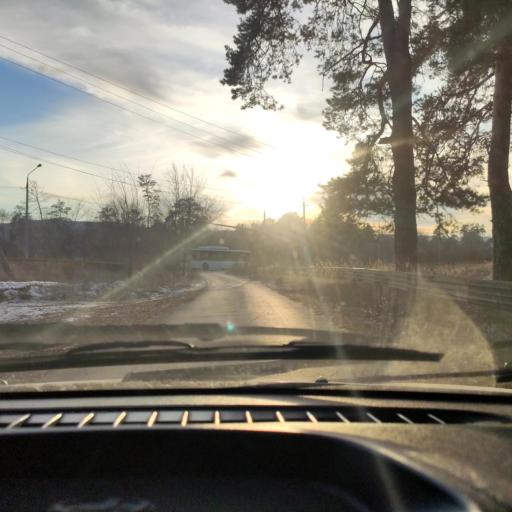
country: RU
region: Samara
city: Zhigulevsk
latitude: 53.4664
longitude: 49.6094
